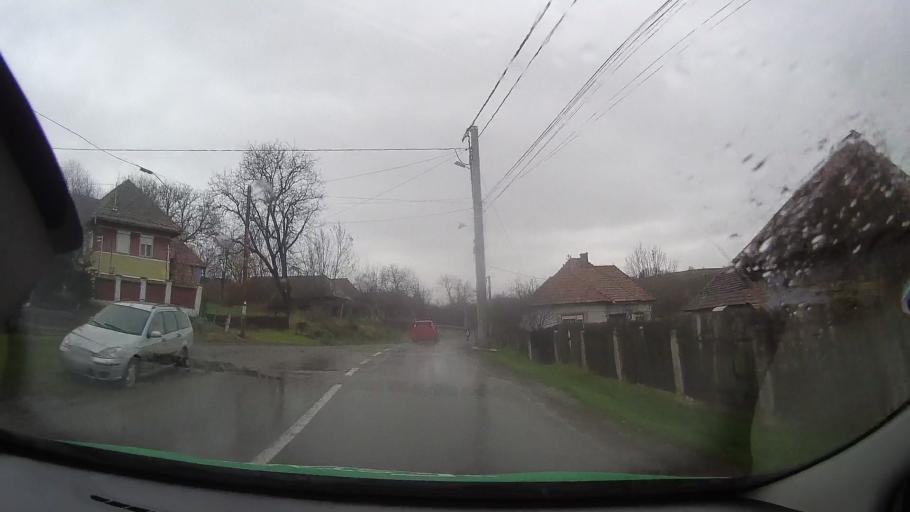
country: RO
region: Mures
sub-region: Comuna Vatava
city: Vatava
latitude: 46.9380
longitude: 24.7676
